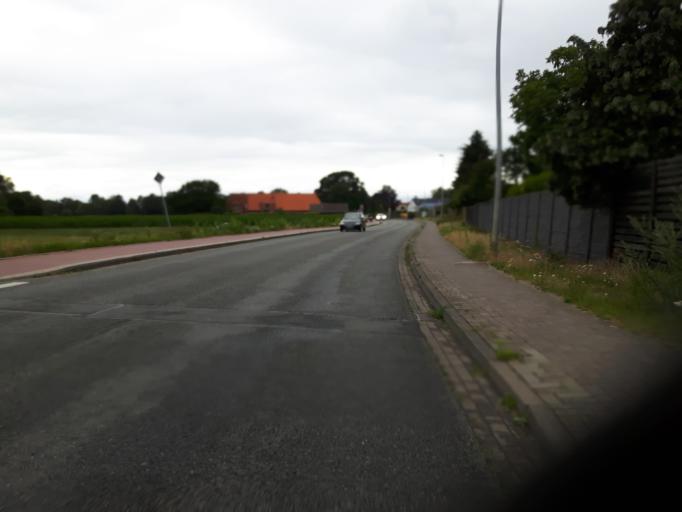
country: DE
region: Lower Saxony
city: Stuhr
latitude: 53.0151
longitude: 8.7753
